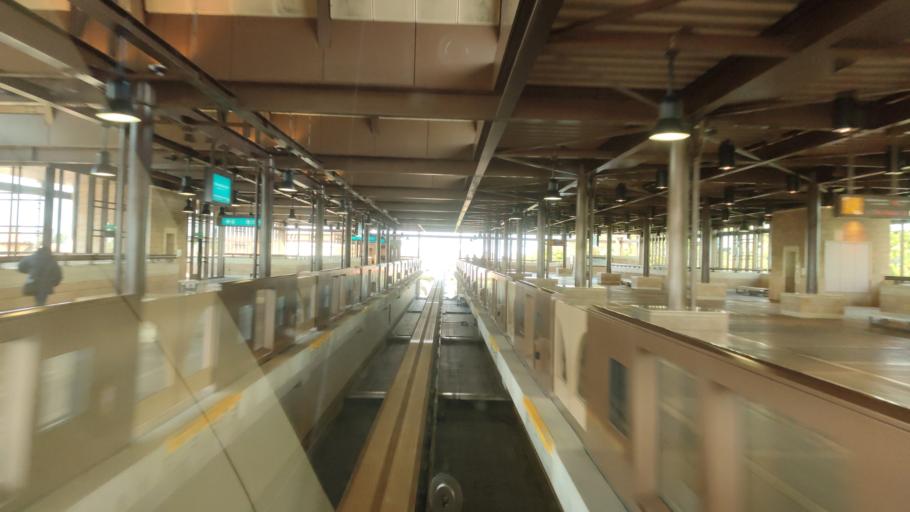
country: JP
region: Tokyo
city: Urayasu
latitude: 35.6273
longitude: 139.8898
